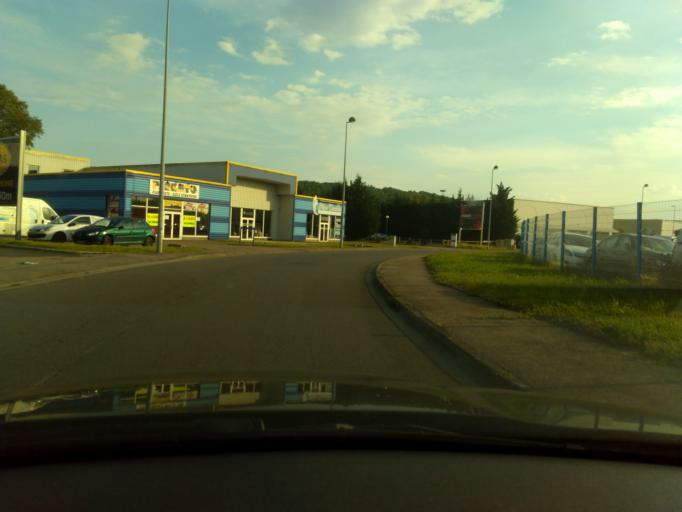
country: FR
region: Lorraine
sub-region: Departement de la Moselle
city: Jouy-aux-Arches
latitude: 49.0768
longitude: 6.0975
